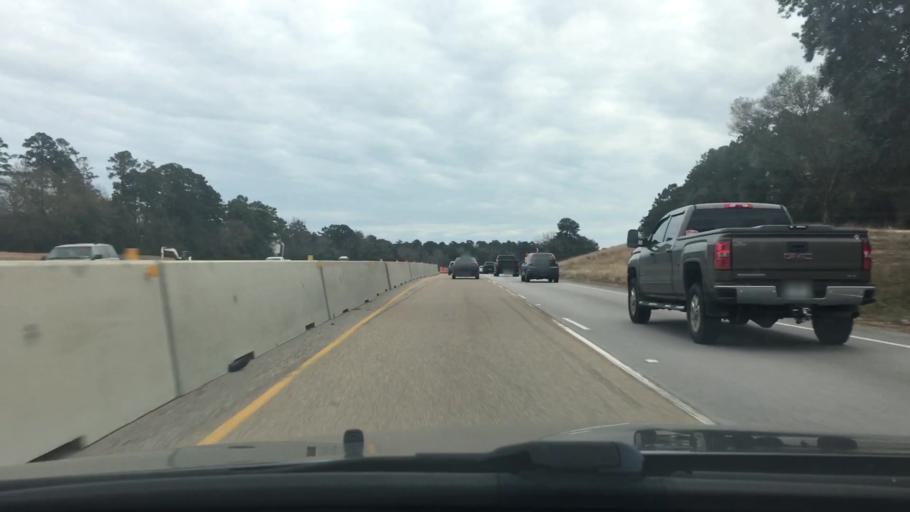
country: US
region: Texas
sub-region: Walker County
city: Huntsville
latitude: 30.6636
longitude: -95.5128
